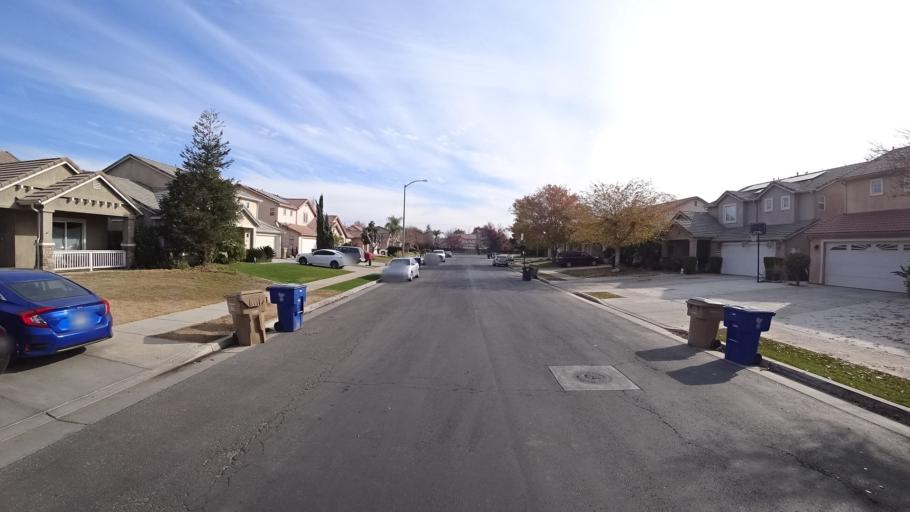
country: US
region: California
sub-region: Kern County
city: Rosedale
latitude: 35.4076
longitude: -119.1299
